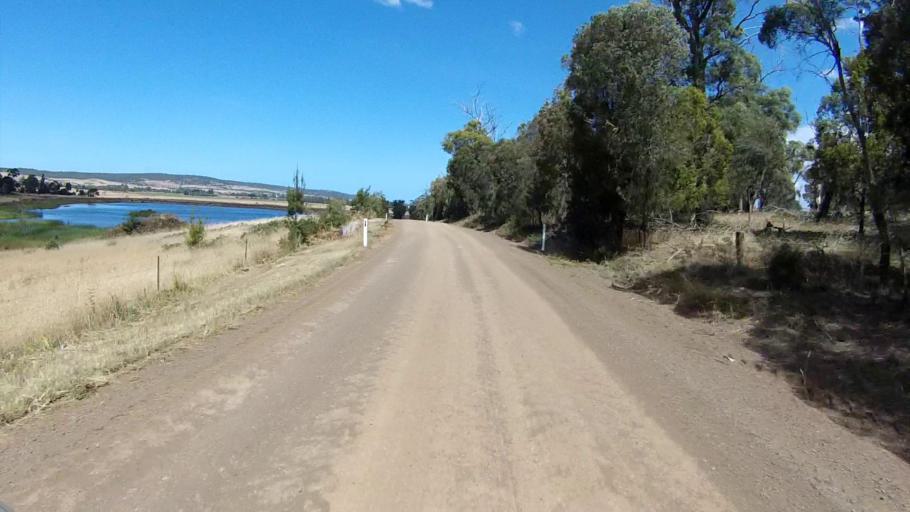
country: AU
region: Tasmania
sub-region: Break O'Day
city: St Helens
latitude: -41.9844
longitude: 148.0656
